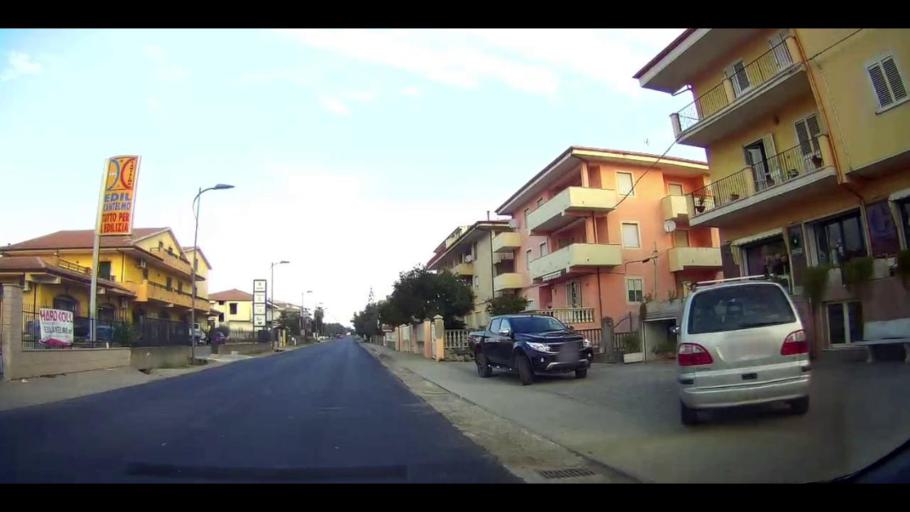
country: IT
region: Calabria
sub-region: Provincia di Crotone
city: Torretta
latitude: 39.4569
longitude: 17.0327
